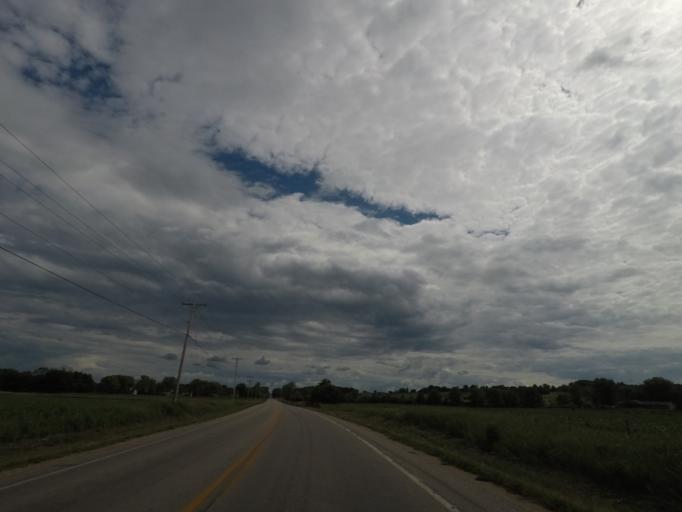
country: US
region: Wisconsin
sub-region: Dane County
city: Belleville
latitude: 42.8467
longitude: -89.5253
